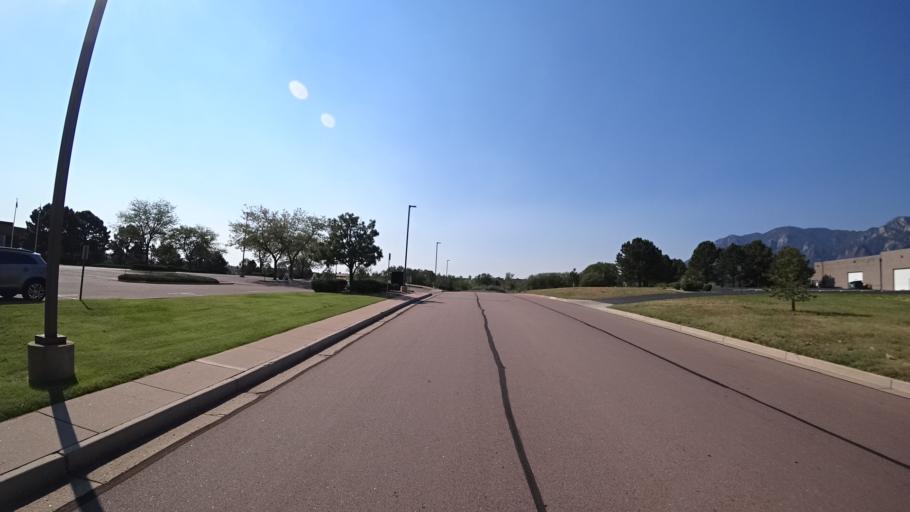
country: US
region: Colorado
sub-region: El Paso County
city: Stratmoor
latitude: 38.7880
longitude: -104.8071
